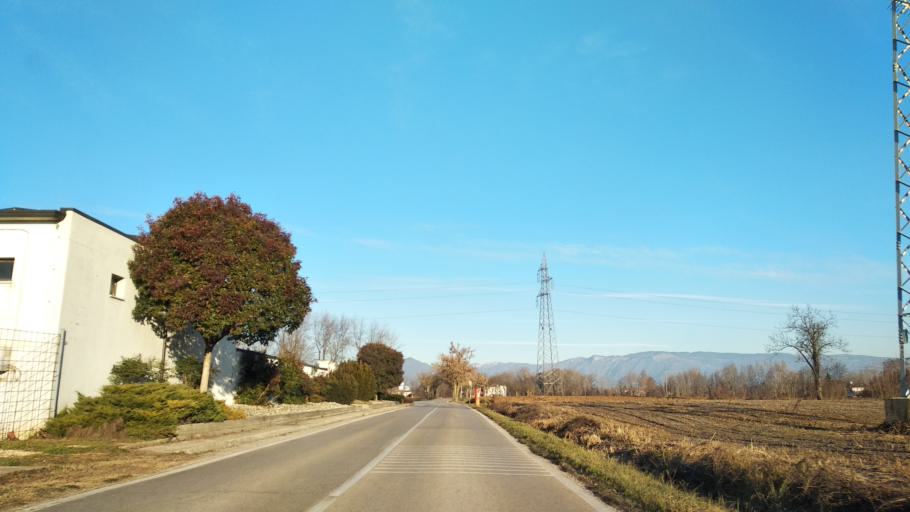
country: IT
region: Veneto
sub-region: Provincia di Vicenza
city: Motta
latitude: 45.5931
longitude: 11.5061
